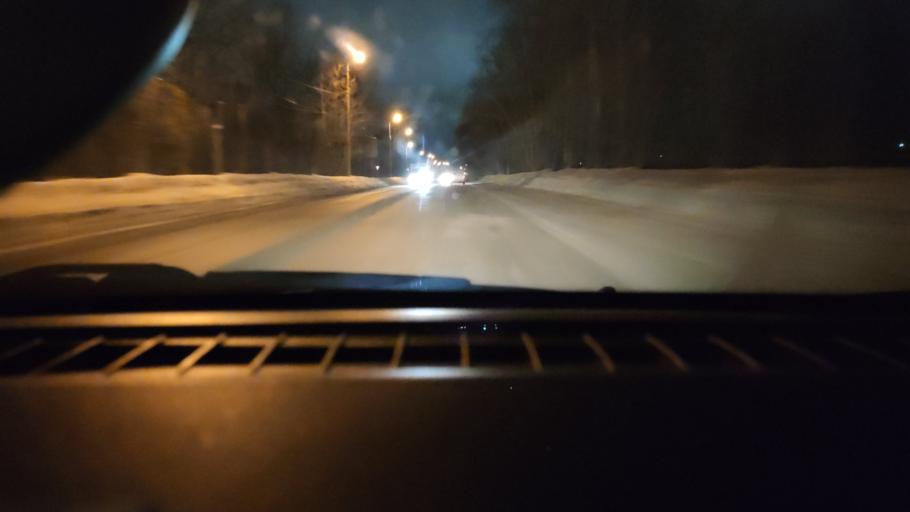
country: RU
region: Perm
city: Krasnokamsk
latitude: 58.0645
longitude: 55.7993
